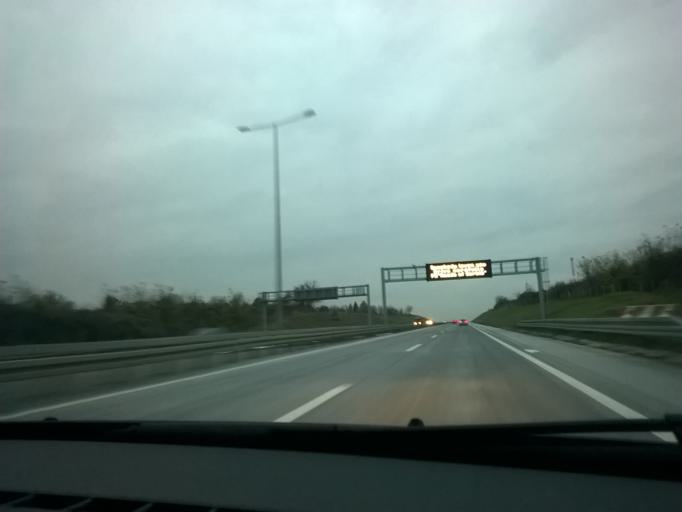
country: RS
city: Beska
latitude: 45.1635
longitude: 20.0807
